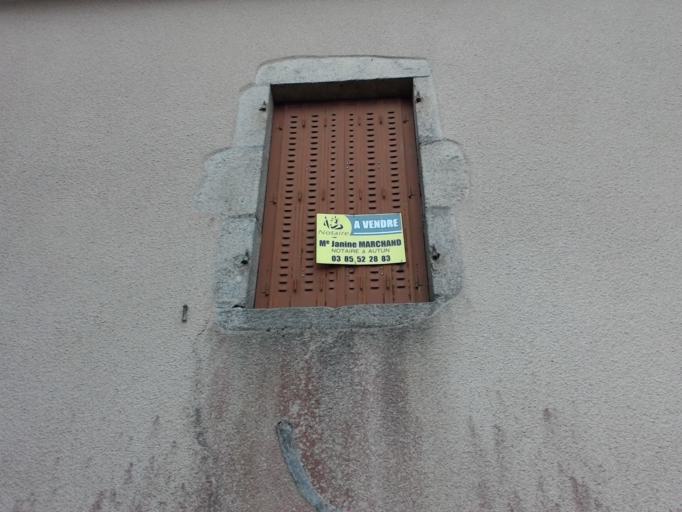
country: FR
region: Bourgogne
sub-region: Departement de la Cote-d'Or
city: Saulieu
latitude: 47.2460
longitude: 4.0630
